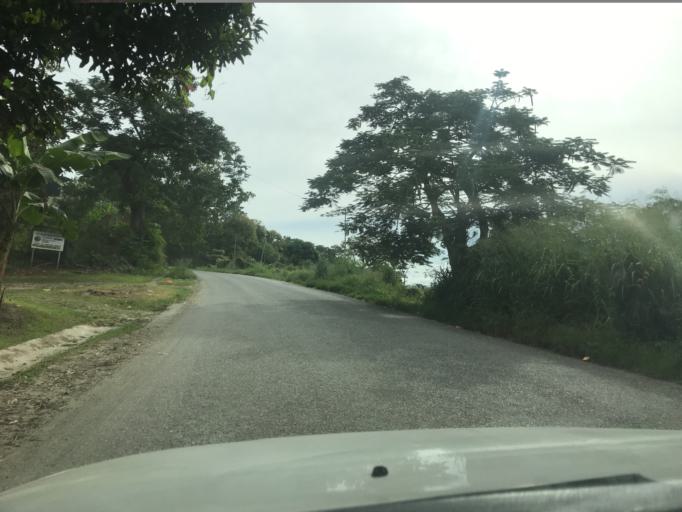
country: SB
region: Guadalcanal
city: Honiara
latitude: -9.4315
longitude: 159.9483
